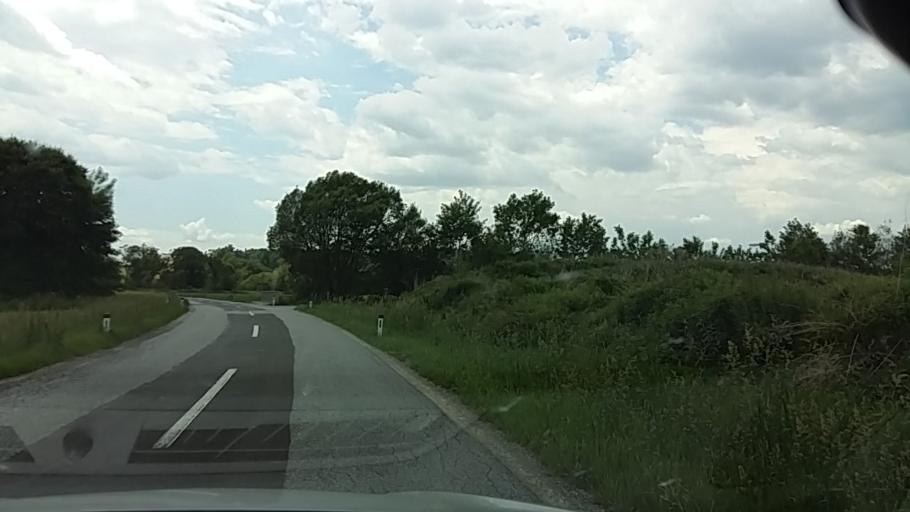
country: AT
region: Styria
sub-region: Politischer Bezirk Hartberg-Fuerstenfeld
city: Hainersdorf
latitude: 47.0984
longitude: 15.9623
